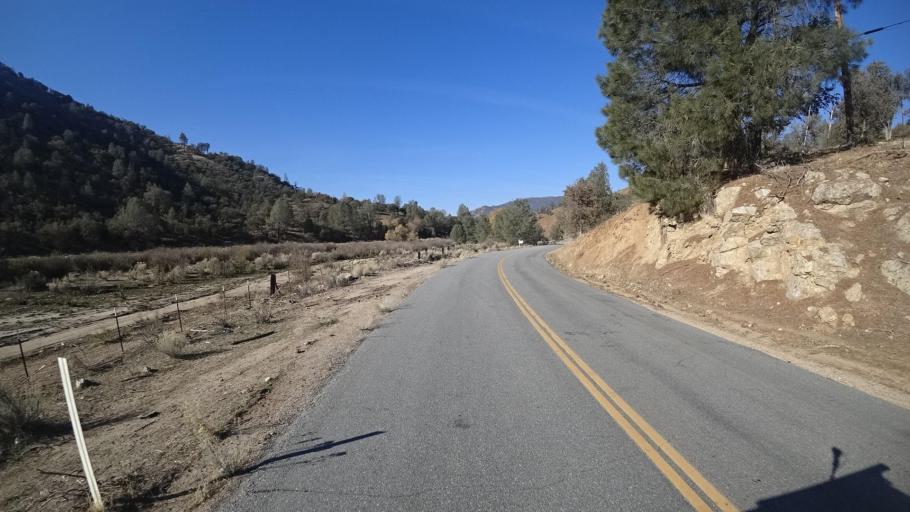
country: US
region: California
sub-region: Kern County
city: Tehachapi
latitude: 35.3064
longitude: -118.4254
